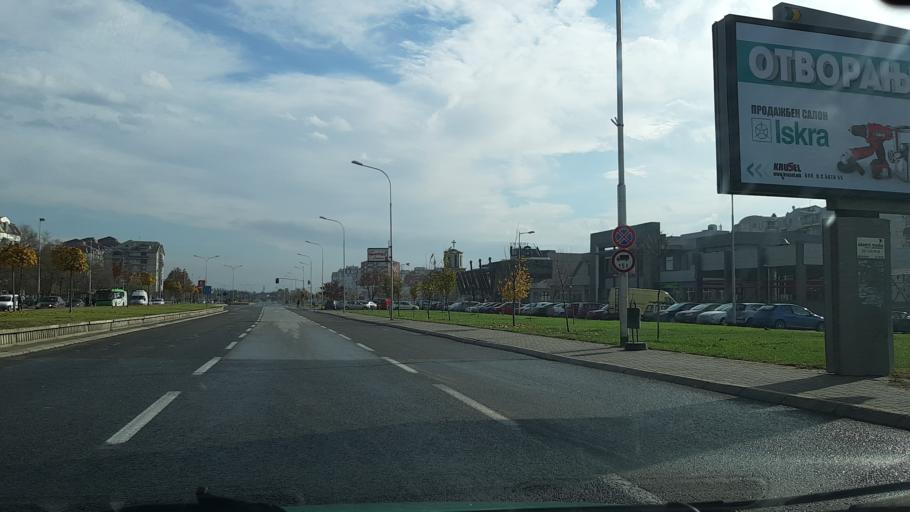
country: MK
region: Kisela Voda
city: Usje
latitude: 41.9824
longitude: 21.4715
